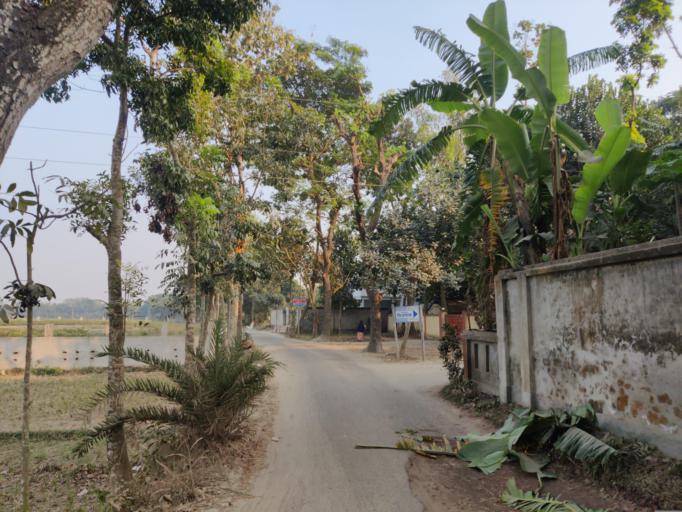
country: BD
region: Dhaka
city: Narsingdi
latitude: 24.0952
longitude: 90.7072
